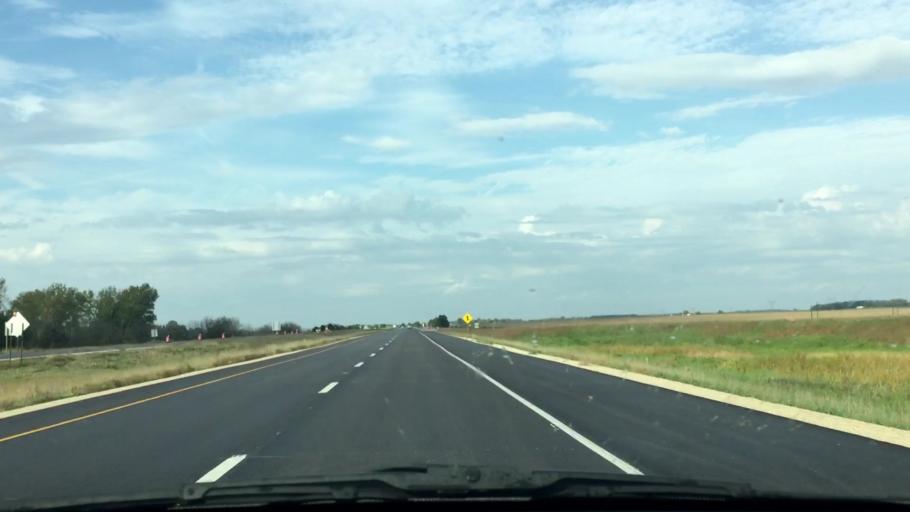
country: US
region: Illinois
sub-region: Whiteside County
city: Erie
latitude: 41.6891
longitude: -90.0995
